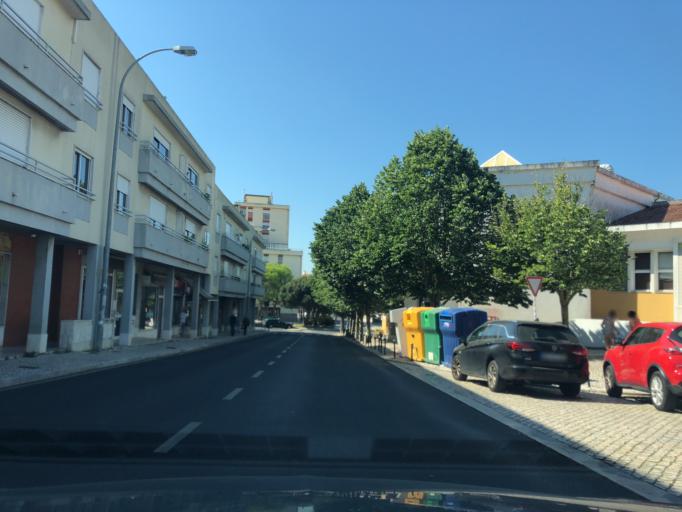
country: PT
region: Lisbon
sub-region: Oeiras
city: Quejas
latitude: 38.7204
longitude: -9.2632
